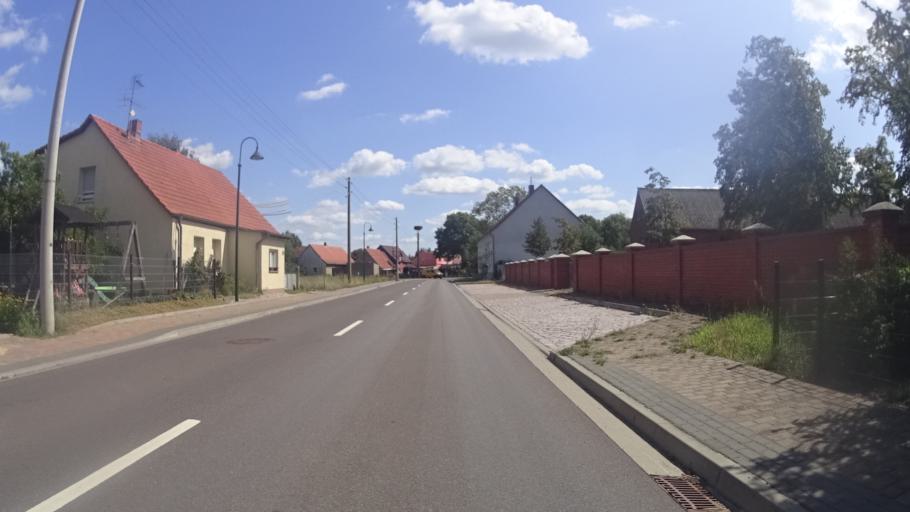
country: DE
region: Saxony-Anhalt
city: Kamern
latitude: 52.7851
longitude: 12.1929
